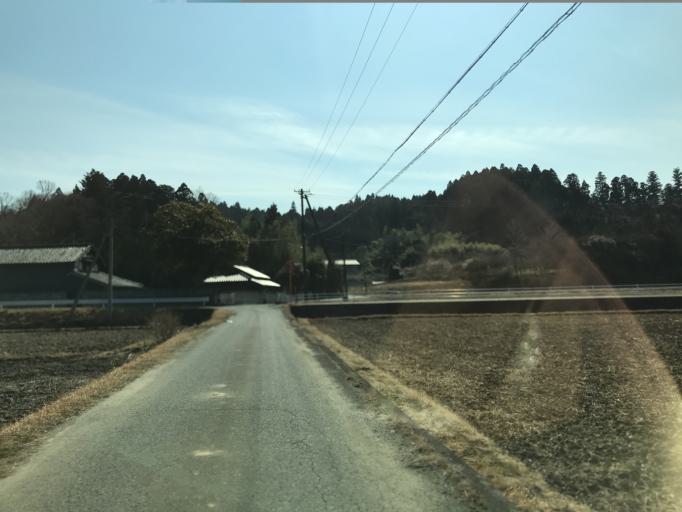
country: JP
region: Fukushima
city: Iwaki
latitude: 37.0472
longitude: 140.9423
